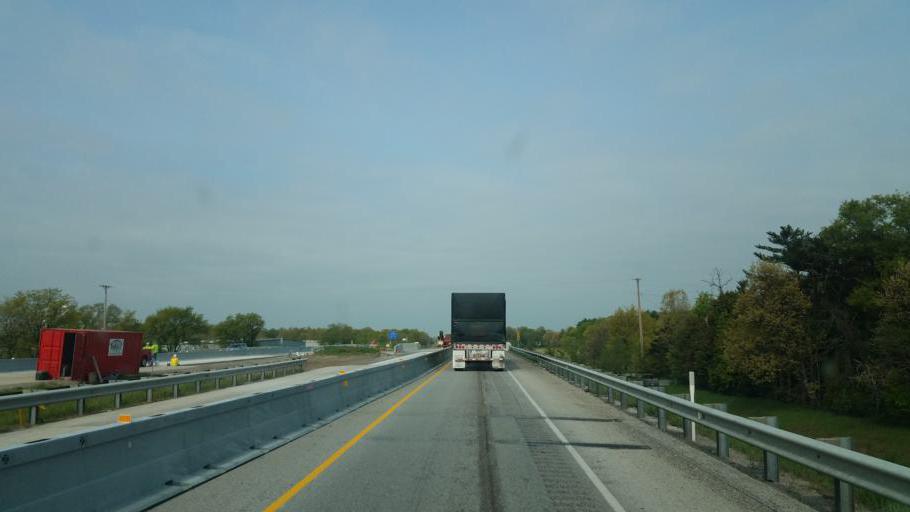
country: US
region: Indiana
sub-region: Elkhart County
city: Simonton Lake
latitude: 41.7307
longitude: -85.9453
